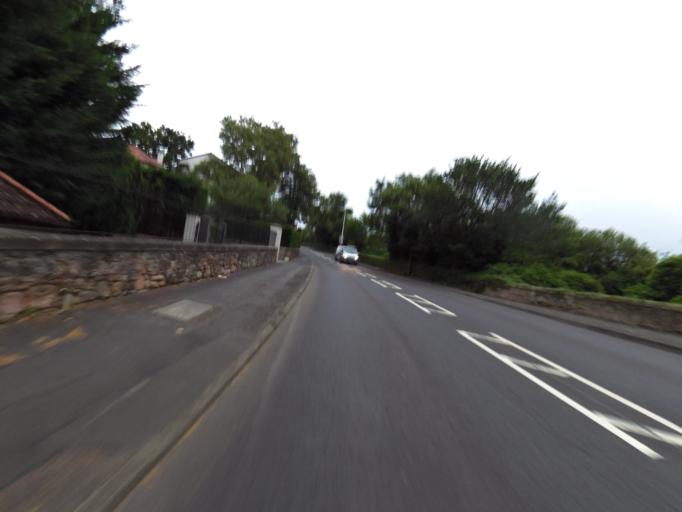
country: GB
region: Scotland
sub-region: East Lothian
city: Musselburgh
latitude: 55.9321
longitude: -3.0593
